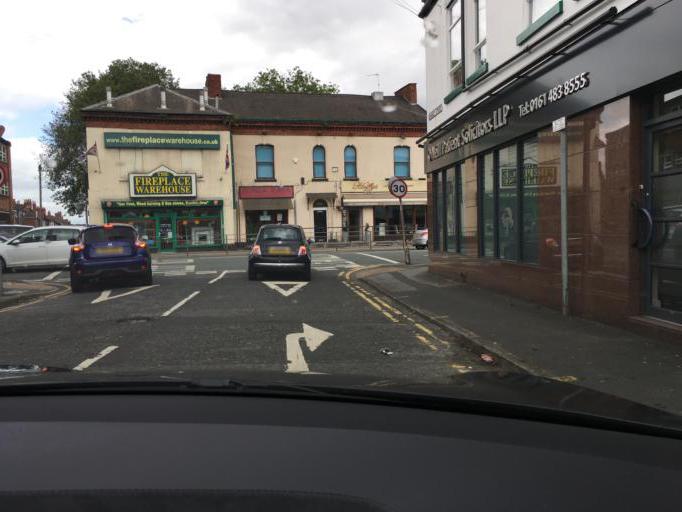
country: GB
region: England
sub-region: Borough of Stockport
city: Hazel Grove
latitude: 53.3790
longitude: -2.1197
